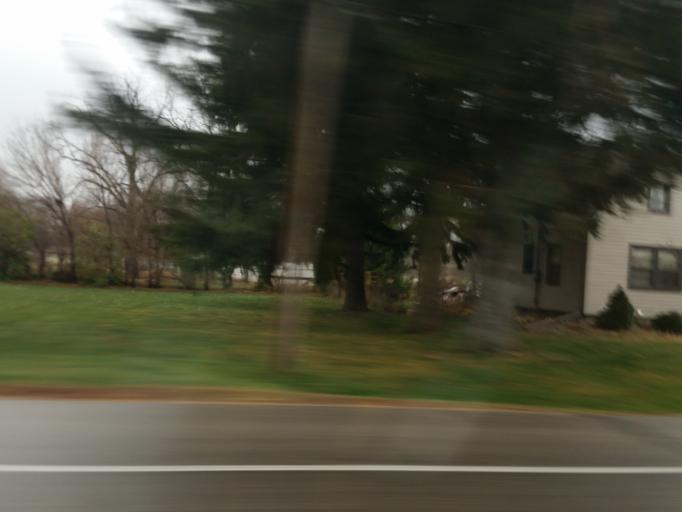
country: US
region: Iowa
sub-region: Black Hawk County
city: Elk Run Heights
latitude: 42.4132
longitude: -92.2686
